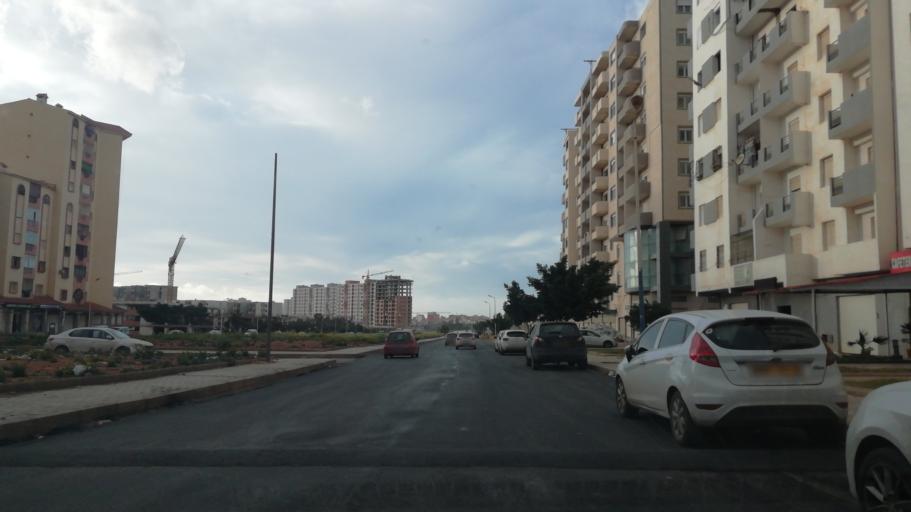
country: DZ
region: Oran
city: Bir el Djir
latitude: 35.7104
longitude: -0.5671
